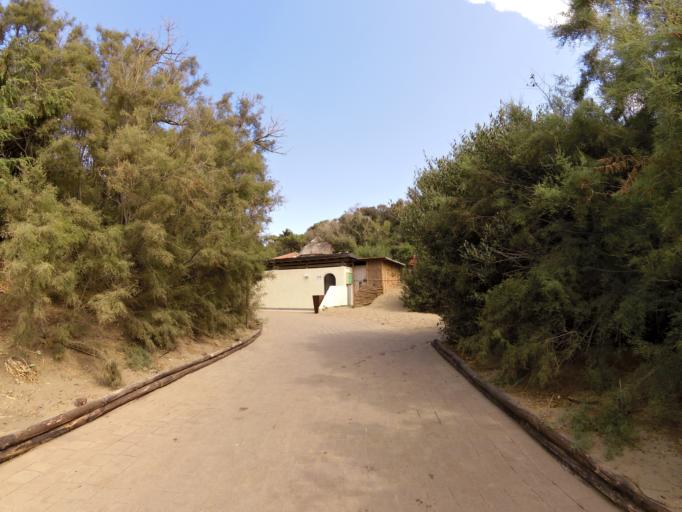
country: IT
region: Tuscany
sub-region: Provincia di Livorno
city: Donoratico
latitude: 43.1532
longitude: 10.5401
